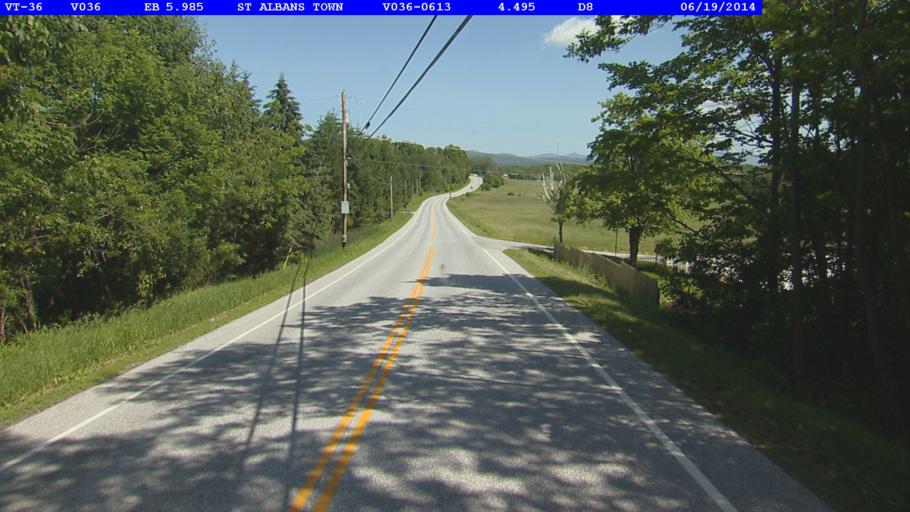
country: US
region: Vermont
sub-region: Franklin County
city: Saint Albans
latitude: 44.7930
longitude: -73.0454
